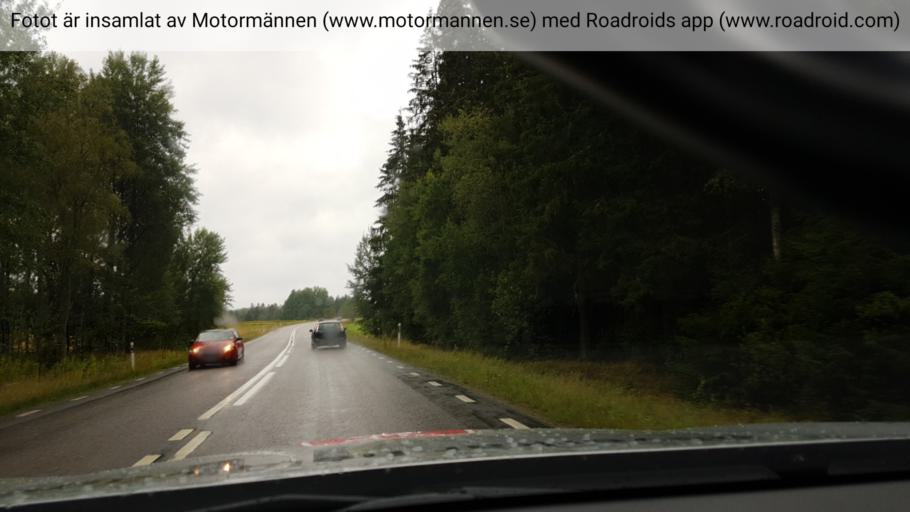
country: SE
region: Vaestra Goetaland
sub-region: Dals-Ed Kommun
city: Ed
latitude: 58.8843
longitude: 11.9060
